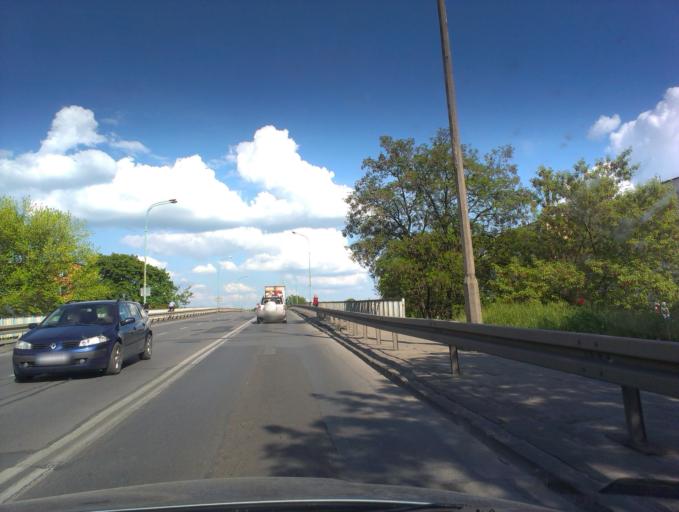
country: PL
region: Masovian Voivodeship
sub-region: Radom
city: Radom
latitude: 51.3993
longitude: 21.1704
